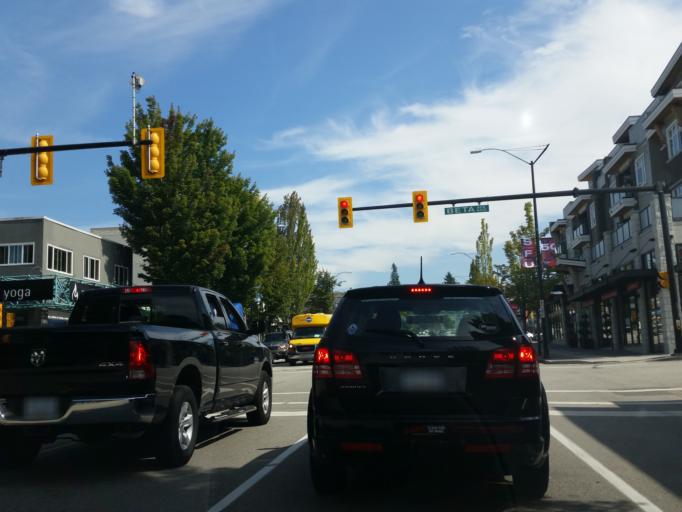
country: CA
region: British Columbia
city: Burnaby
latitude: 49.2810
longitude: -122.9978
